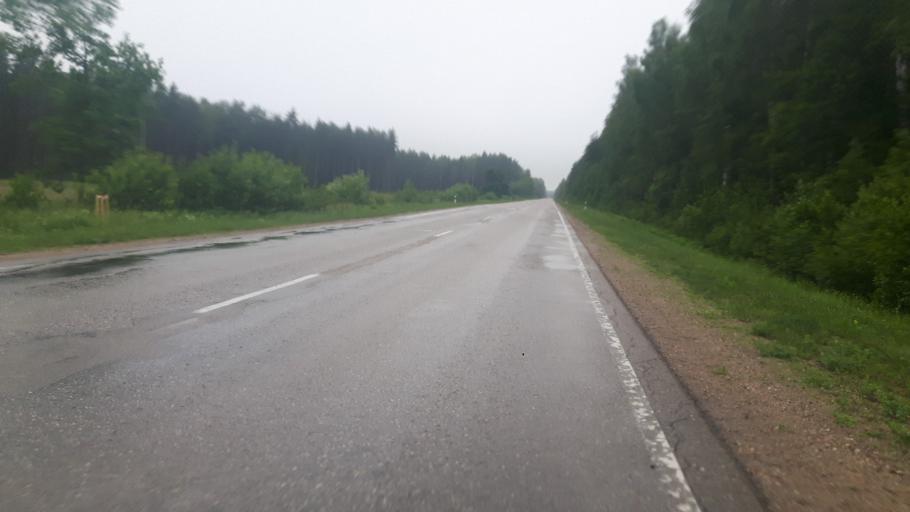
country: LV
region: Rucavas
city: Rucava
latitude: 56.1158
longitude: 21.1426
